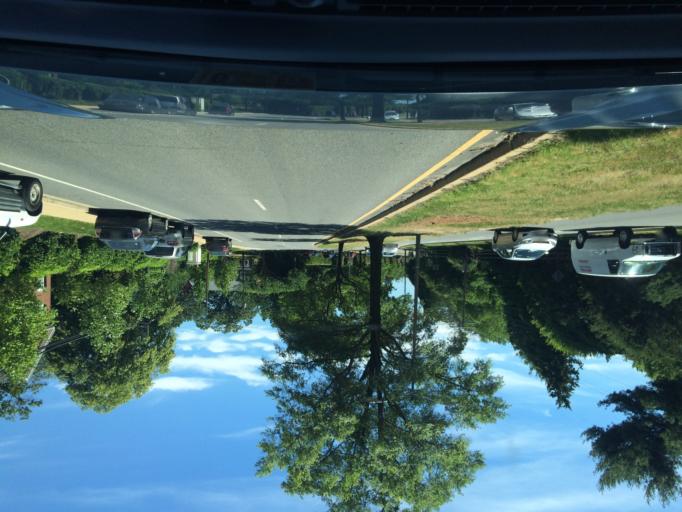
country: US
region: Virginia
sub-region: Fairfax County
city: Huntington
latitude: 38.8358
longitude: -77.0850
